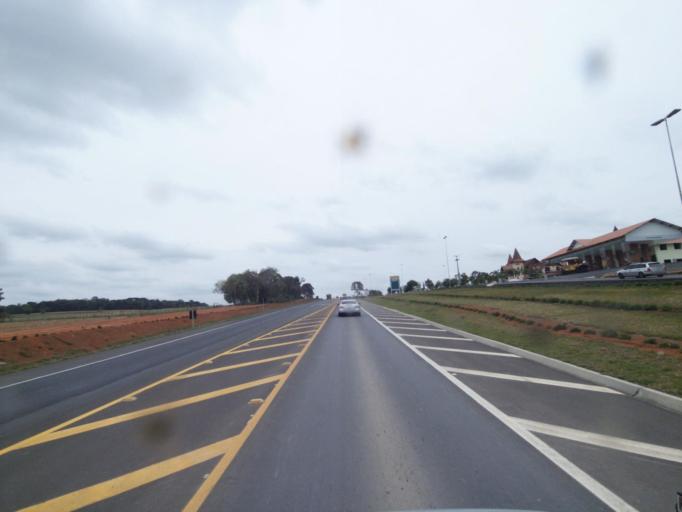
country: BR
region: Parana
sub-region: Irati
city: Irati
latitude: -25.4642
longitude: -50.5664
